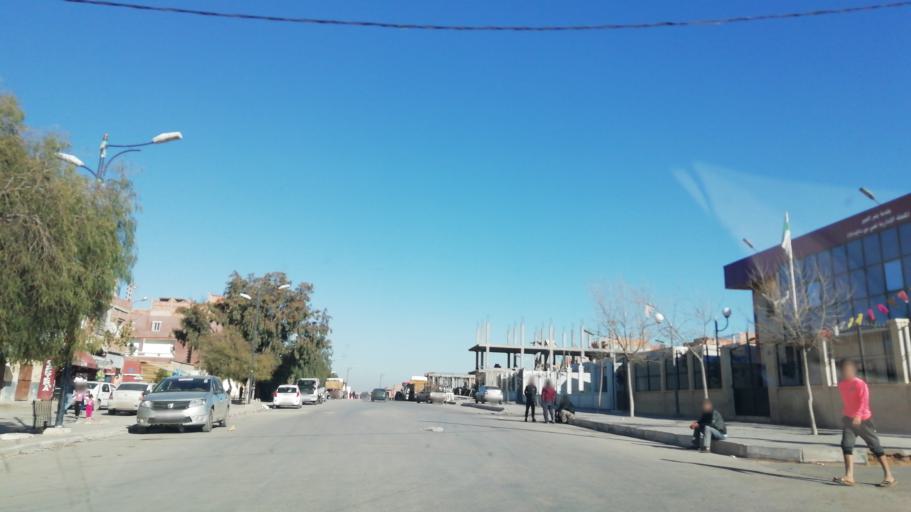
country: DZ
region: Oran
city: Bir el Djir
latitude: 35.7243
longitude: -0.5309
